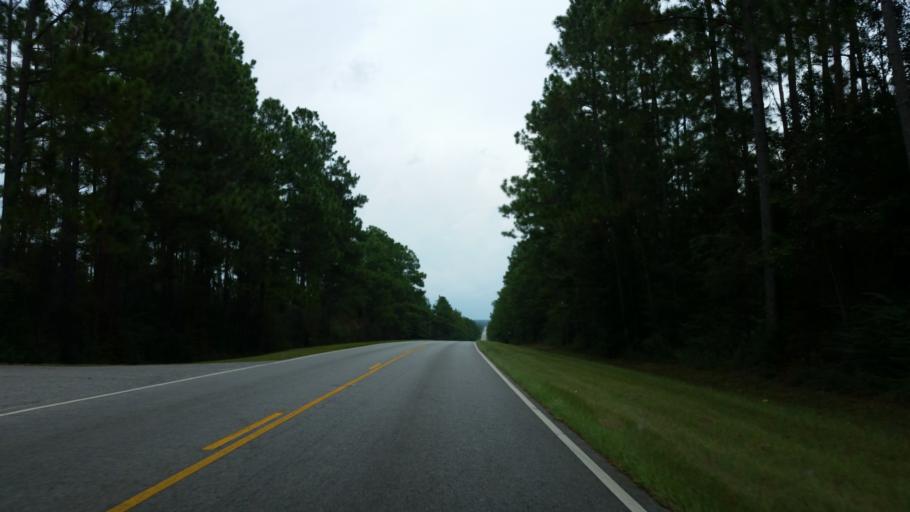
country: US
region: Florida
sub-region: Escambia County
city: Molino
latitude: 30.6620
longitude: -87.2987
